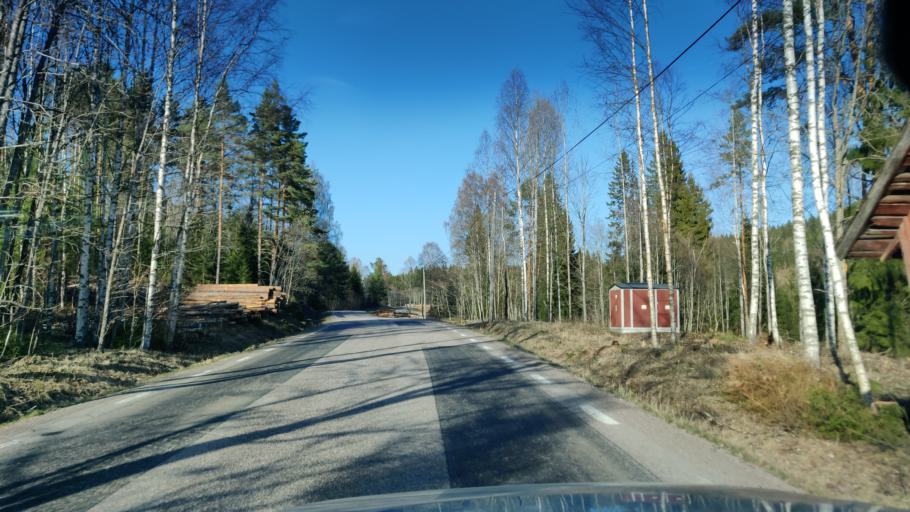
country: SE
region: Vaermland
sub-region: Sunne Kommun
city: Sunne
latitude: 59.9844
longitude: 13.2640
